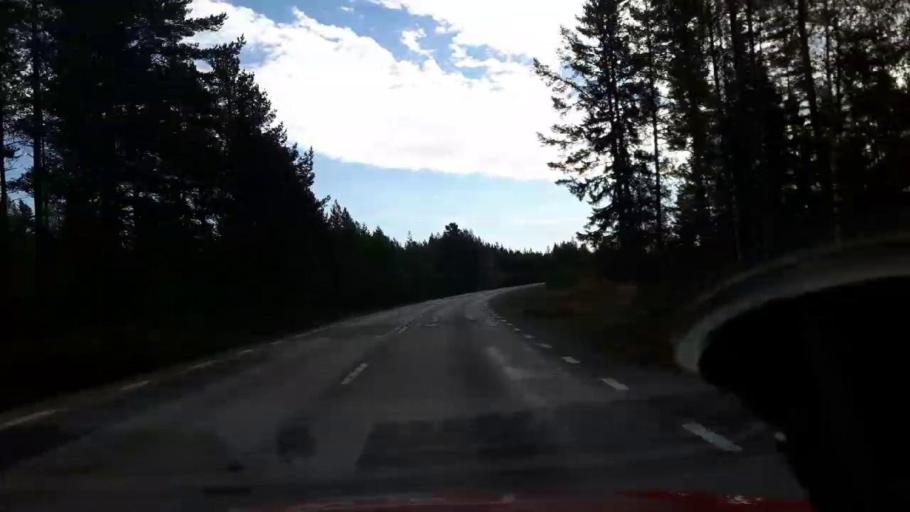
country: SE
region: Gaevleborg
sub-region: Ljusdals Kommun
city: Farila
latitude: 61.9733
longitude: 15.3416
